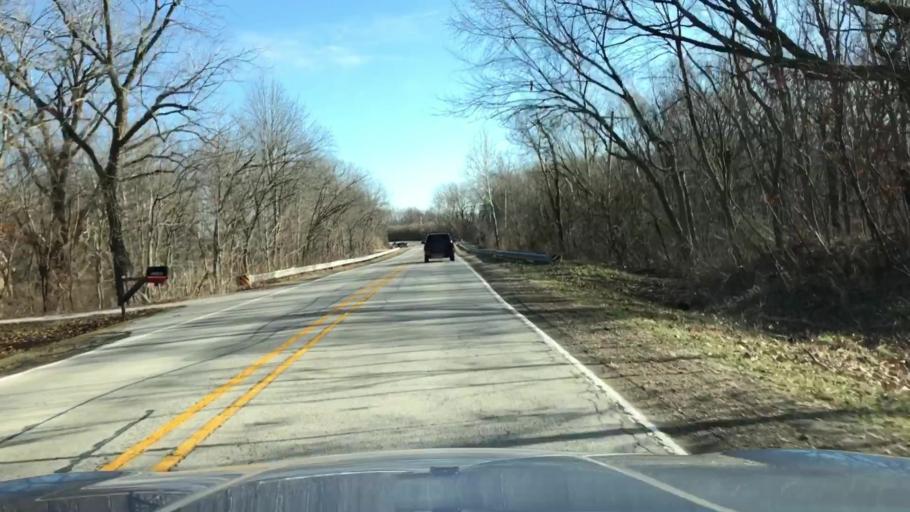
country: US
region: Illinois
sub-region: McLean County
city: Lexington
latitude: 40.6469
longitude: -88.8391
